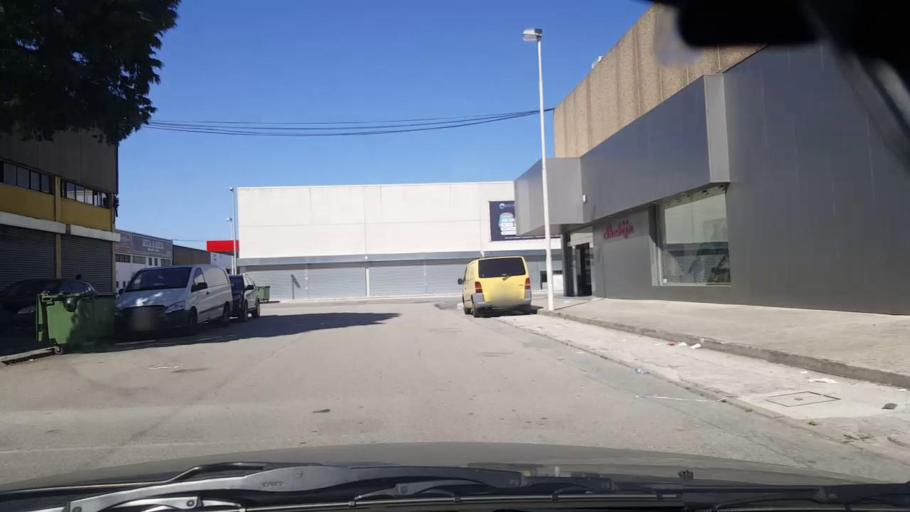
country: PT
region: Porto
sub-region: Vila do Conde
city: Arvore
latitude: 41.3279
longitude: -8.7123
